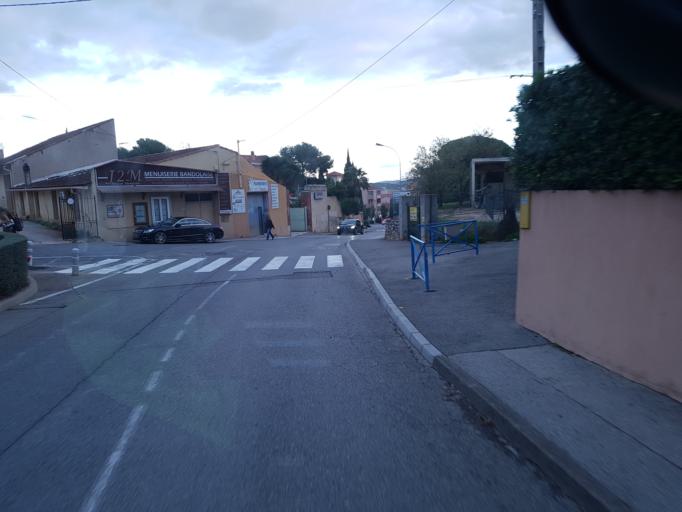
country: FR
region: Provence-Alpes-Cote d'Azur
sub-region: Departement du Var
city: Bandol
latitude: 43.1395
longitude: 5.7497
